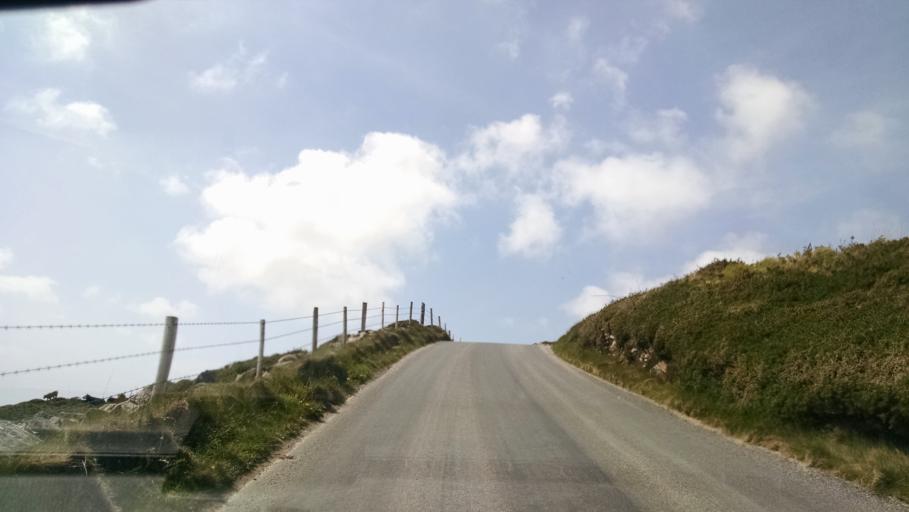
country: IE
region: Connaught
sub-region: County Galway
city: Clifden
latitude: 53.4988
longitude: -10.0896
